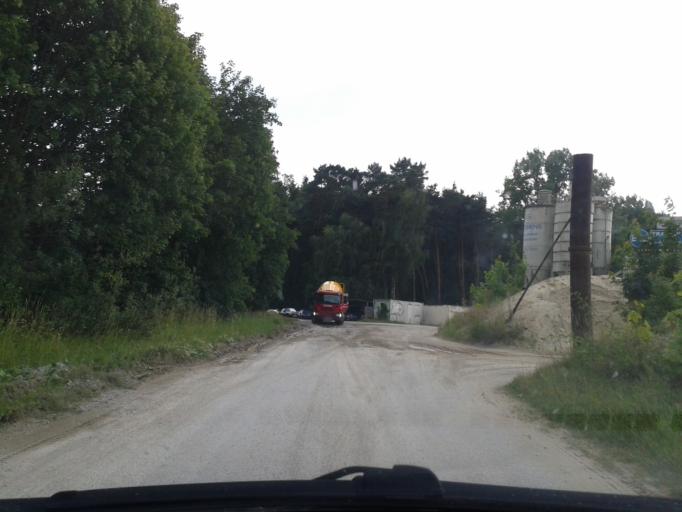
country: DE
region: North Rhine-Westphalia
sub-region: Regierungsbezirk Detmold
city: Hovelhof
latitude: 51.7590
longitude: 8.6928
